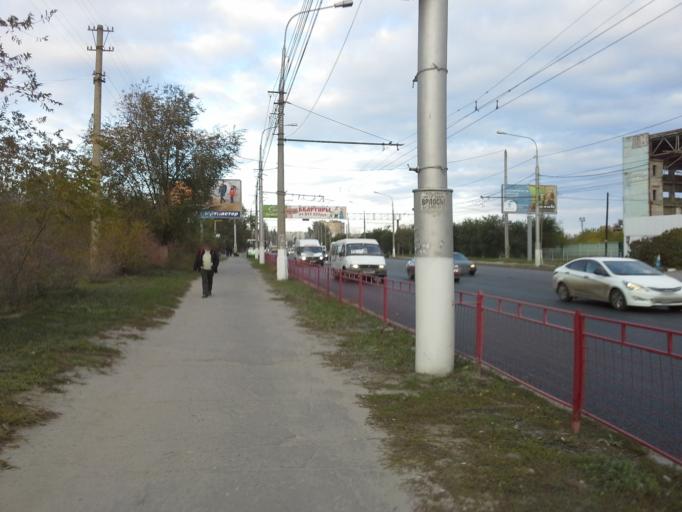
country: RU
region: Volgograd
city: Vodstroy
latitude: 48.8061
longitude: 44.6079
